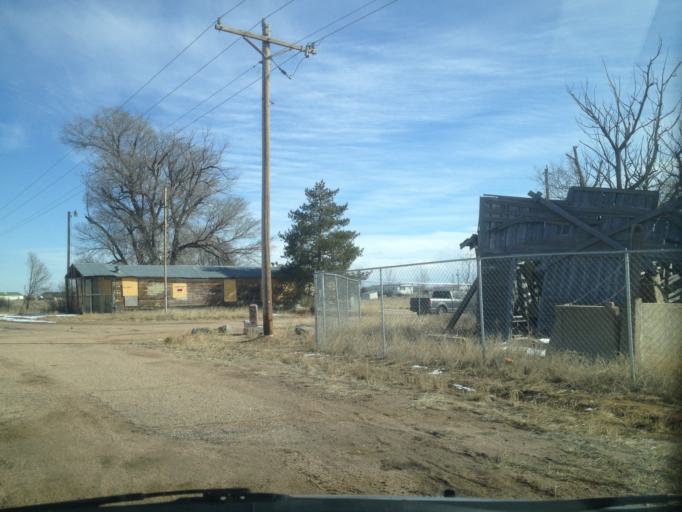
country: US
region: Colorado
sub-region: Weld County
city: Kersey
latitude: 40.2908
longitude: -104.2595
